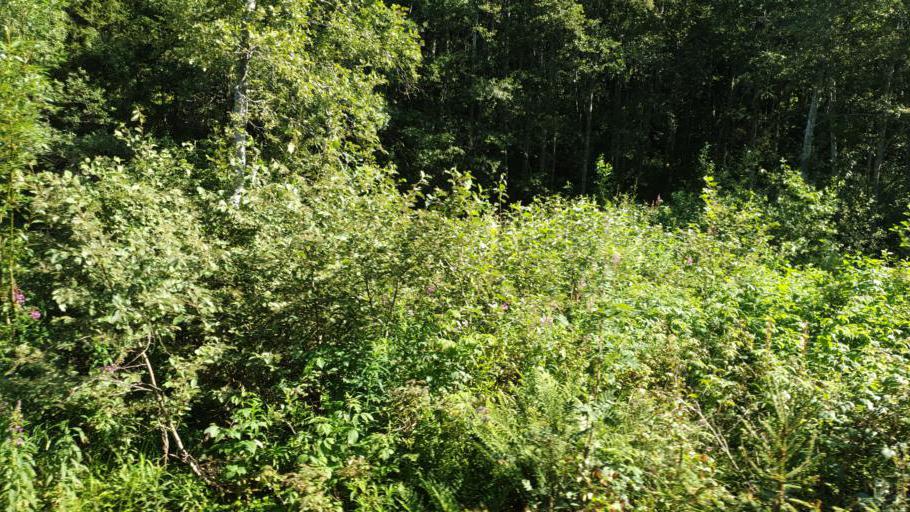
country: NO
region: Sor-Trondelag
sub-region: Orkdal
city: Orkanger
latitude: 63.1853
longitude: 9.7731
